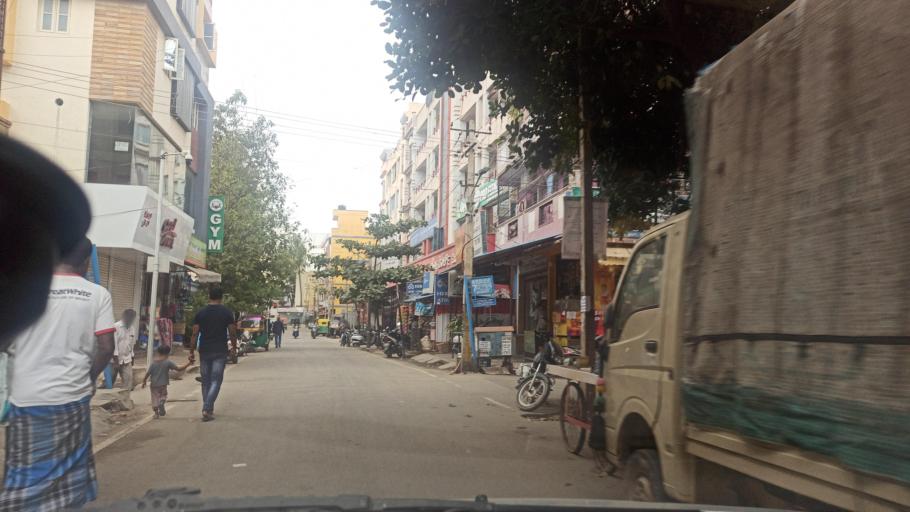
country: IN
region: Karnataka
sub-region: Bangalore Urban
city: Bangalore
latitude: 13.0364
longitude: 77.6051
